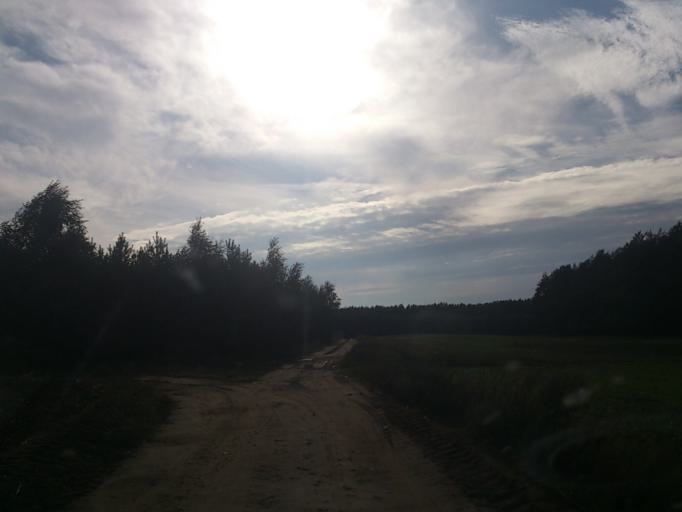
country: PL
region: Kujawsko-Pomorskie
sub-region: Powiat golubsko-dobrzynski
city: Radomin
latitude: 53.1305
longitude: 19.1308
